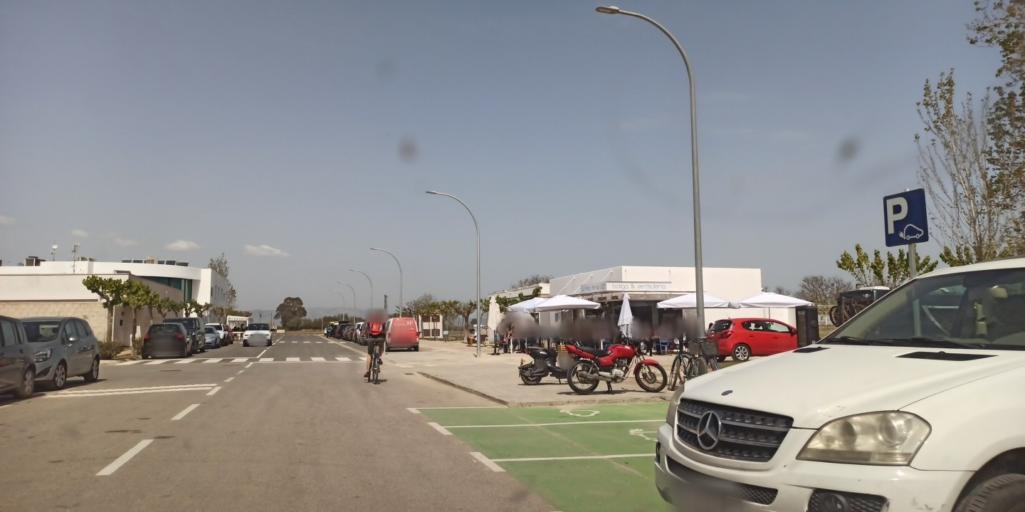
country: ES
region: Catalonia
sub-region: Provincia de Tarragona
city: Deltebre
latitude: 40.6462
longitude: 0.6883
